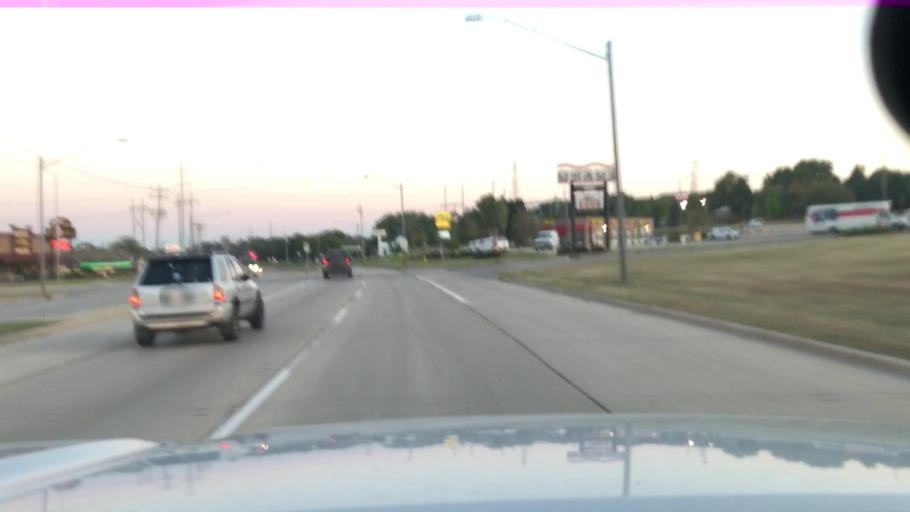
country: US
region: Wisconsin
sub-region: Brown County
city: Allouez
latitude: 44.4860
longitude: -87.9712
